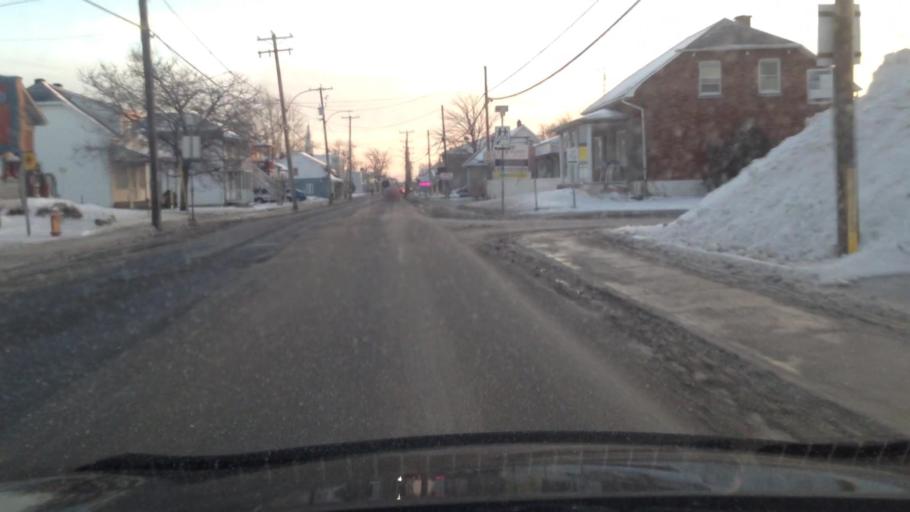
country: CA
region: Quebec
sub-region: Lanaudiere
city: Saint-Lin-Laurentides
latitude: 45.8595
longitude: -73.7571
